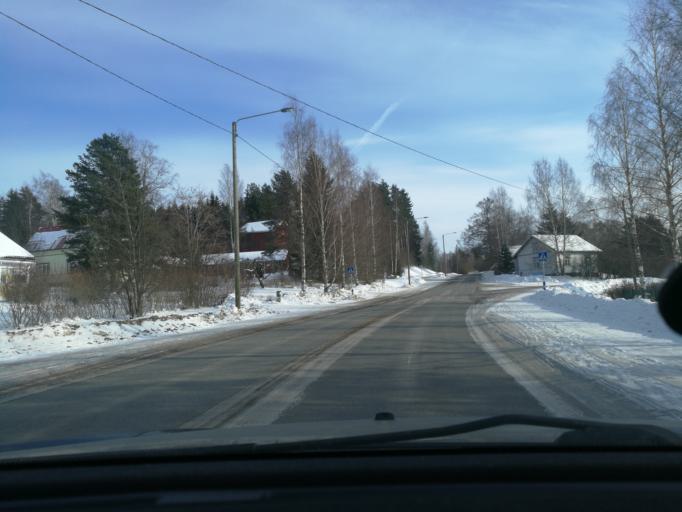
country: FI
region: Uusimaa
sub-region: Helsinki
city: Saukkola
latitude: 60.4732
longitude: 23.9867
